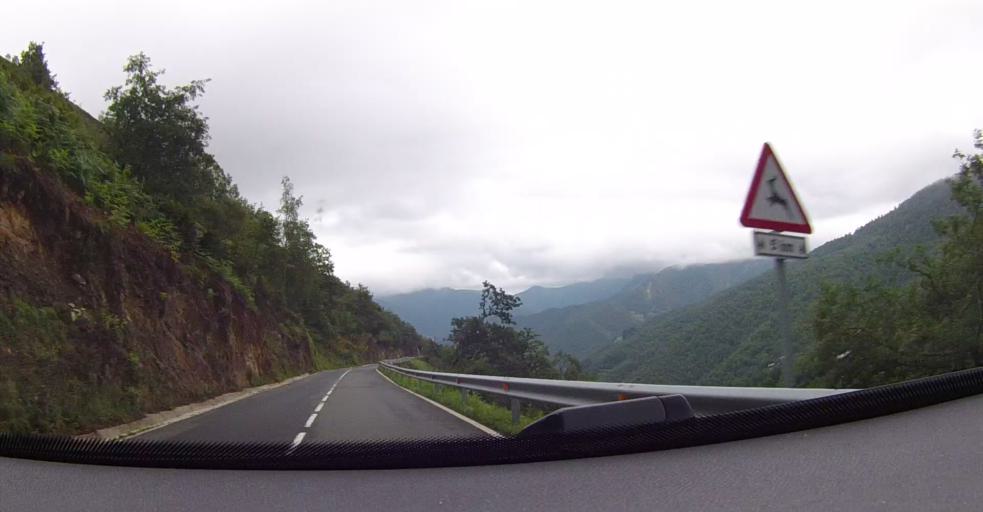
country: ES
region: Cantabria
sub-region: Provincia de Cantabria
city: Camaleno
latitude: 43.0957
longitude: -4.7097
